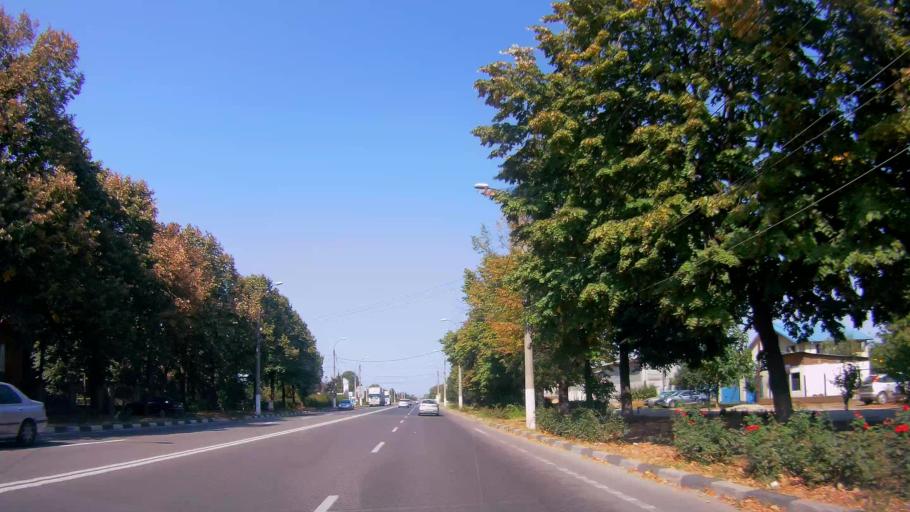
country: RO
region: Giurgiu
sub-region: Comuna Fratesti
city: Remus
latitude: 43.9305
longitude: 25.9758
